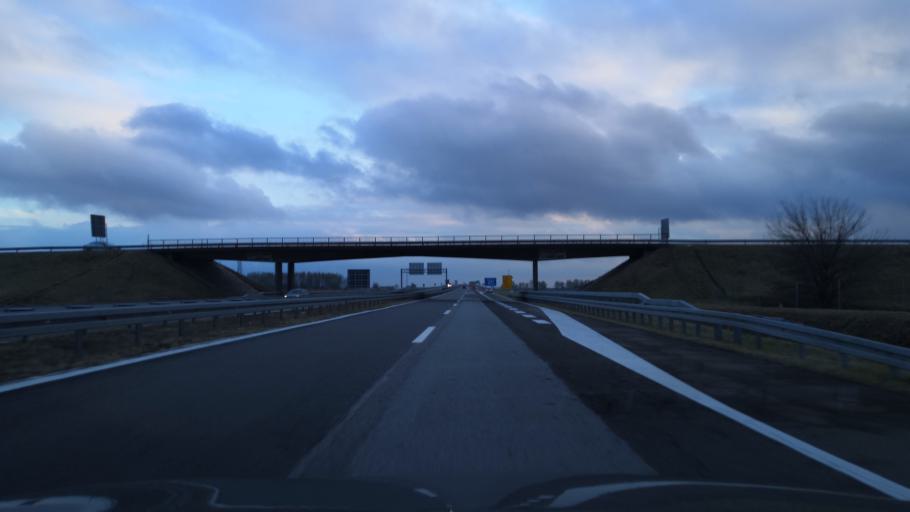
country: RS
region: Autonomna Pokrajina Vojvodina
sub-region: Juznobacki Okrug
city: Vrbas
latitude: 45.5555
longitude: 19.7198
